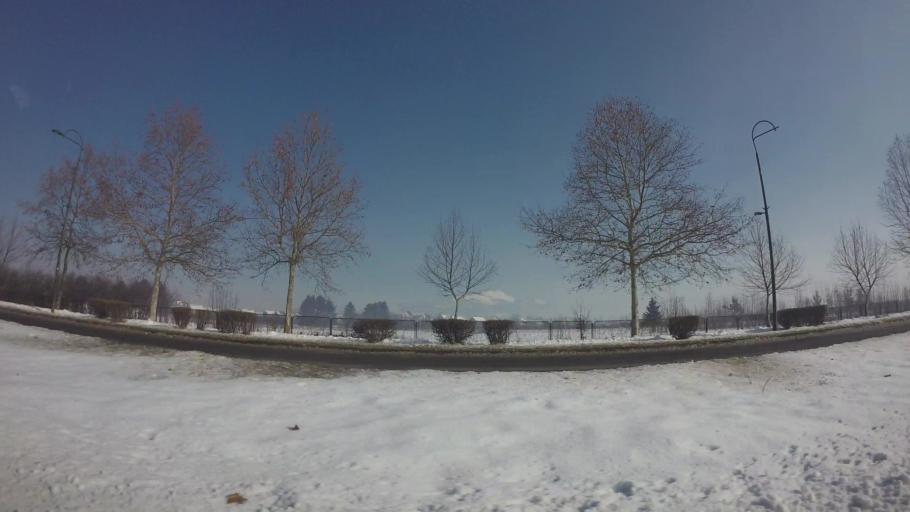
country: BA
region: Federation of Bosnia and Herzegovina
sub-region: Kanton Sarajevo
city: Sarajevo
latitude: 43.8064
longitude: 18.3112
